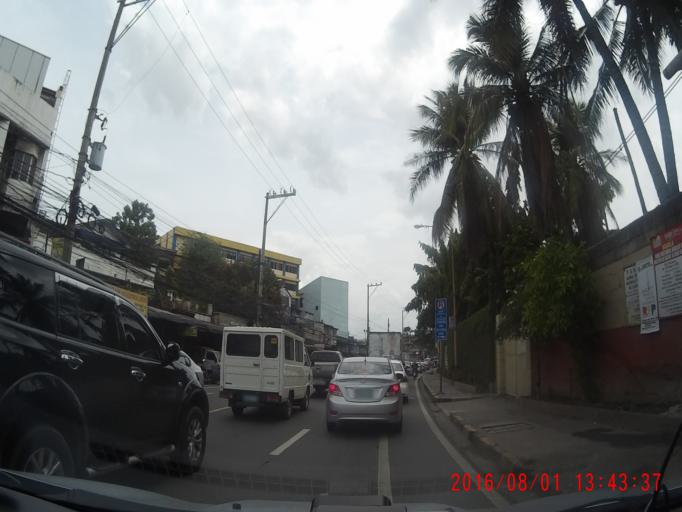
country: PH
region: Metro Manila
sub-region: Pasig
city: Pasig City
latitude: 14.5673
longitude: 121.0801
